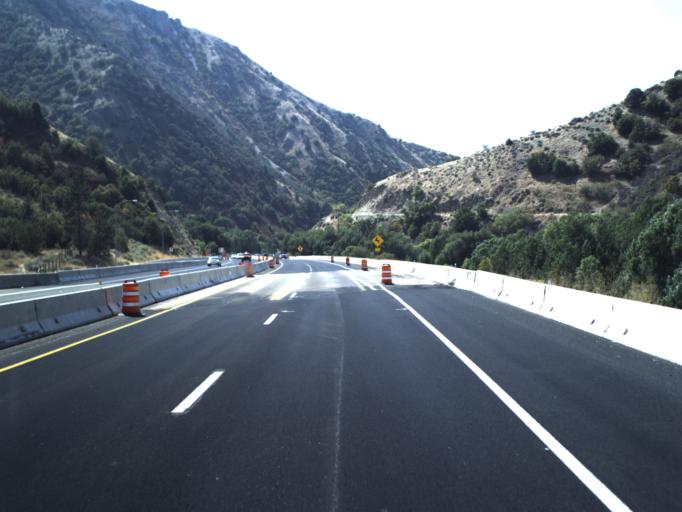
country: US
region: Utah
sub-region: Box Elder County
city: Brigham City
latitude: 41.4982
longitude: -111.9535
